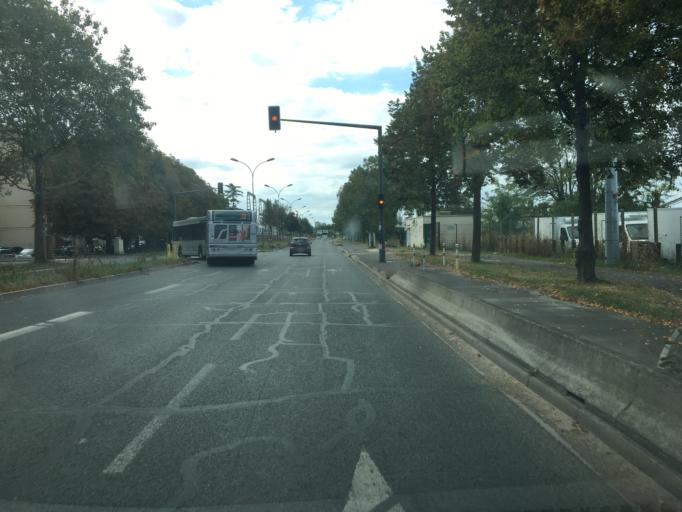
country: FR
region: Ile-de-France
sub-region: Departement du Val-de-Marne
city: Valenton
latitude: 48.7539
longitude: 2.4495
